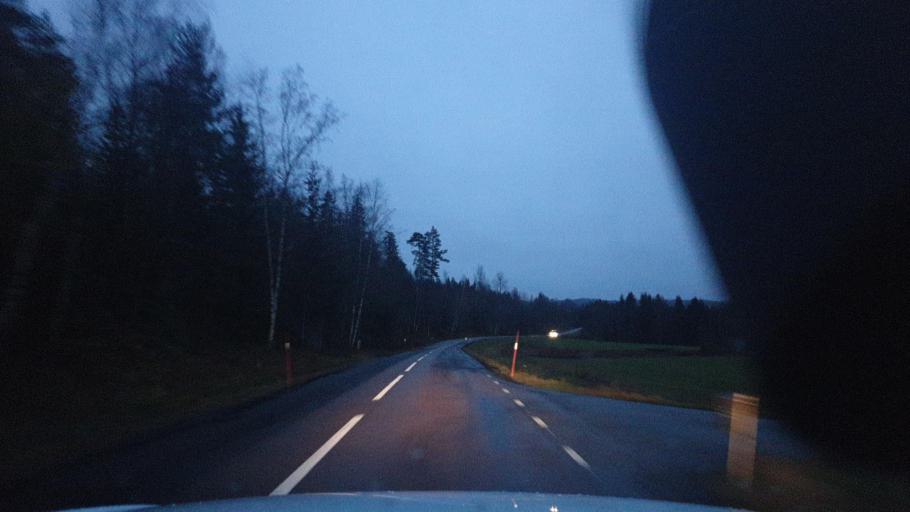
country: SE
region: Vaermland
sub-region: Eda Kommun
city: Amotfors
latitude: 59.7587
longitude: 12.2133
